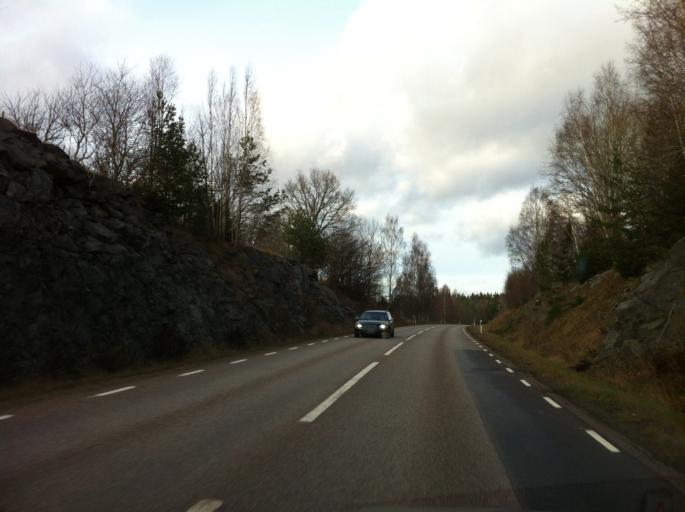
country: SE
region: Kronoberg
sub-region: Uppvidinge Kommun
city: Aseda
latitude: 57.1690
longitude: 15.4933
